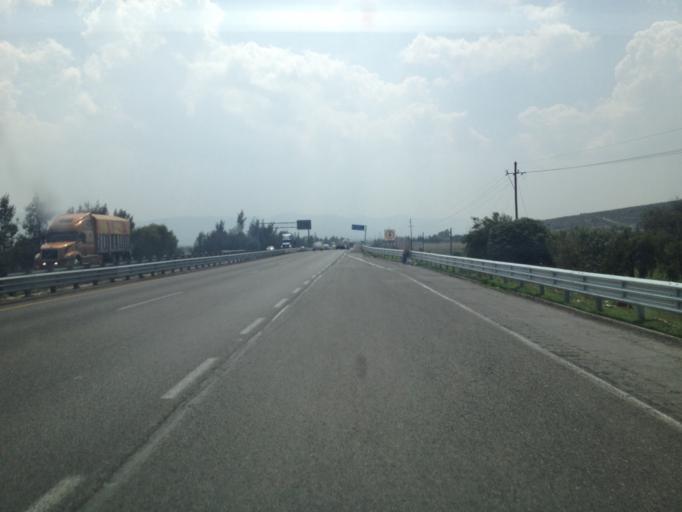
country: MX
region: Puebla
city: Cuacnopalan
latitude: 18.8281
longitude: -97.4953
